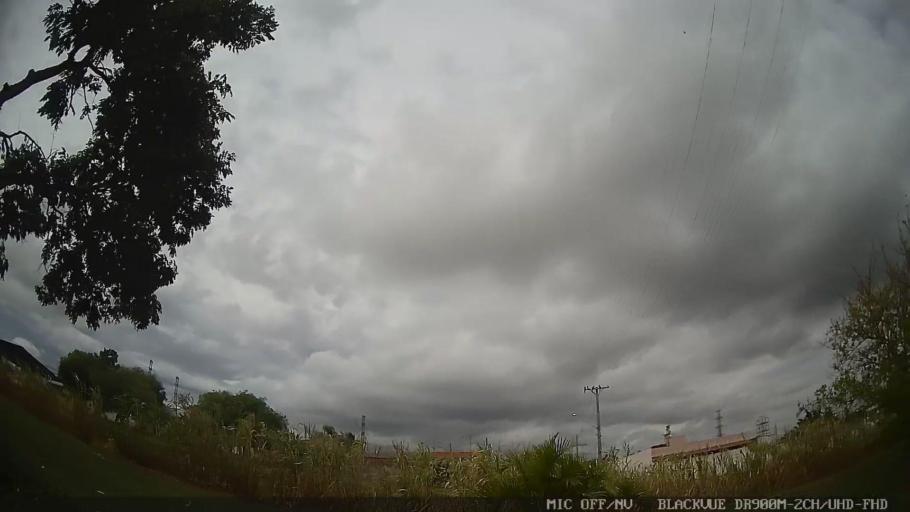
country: BR
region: Sao Paulo
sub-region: Salto
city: Salto
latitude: -23.2130
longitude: -47.2873
